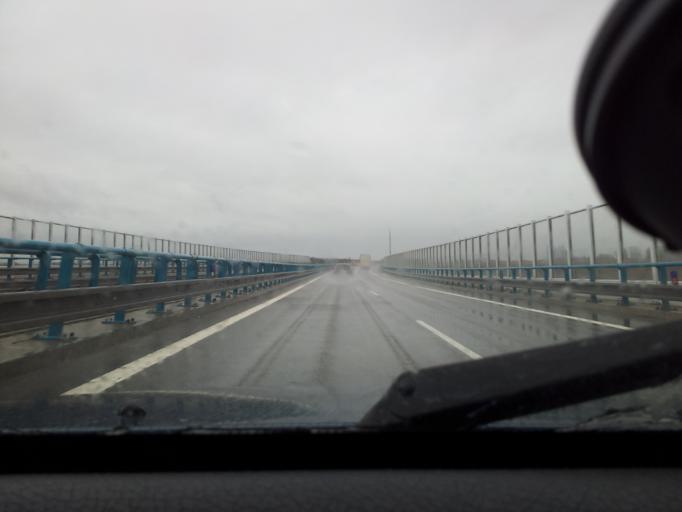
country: SK
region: Nitriansky
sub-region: Okres Nitra
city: Nitra
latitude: 48.3213
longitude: 18.1956
